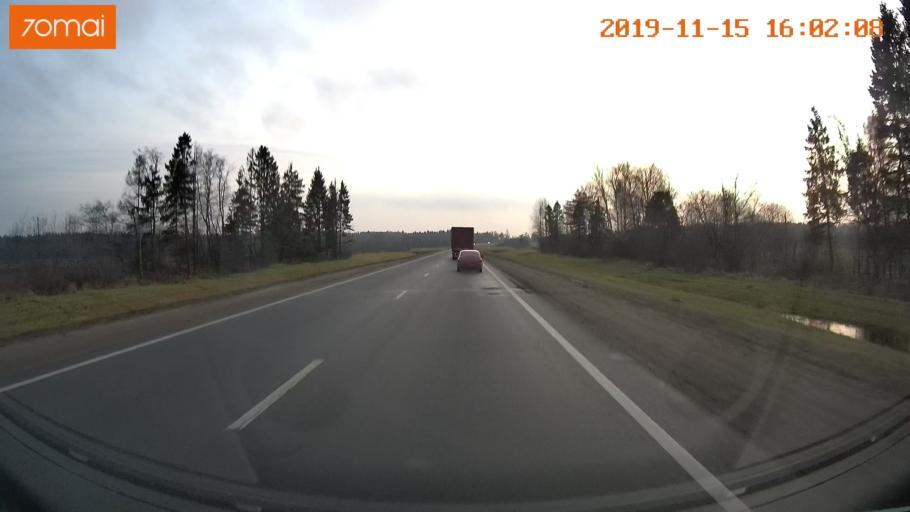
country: RU
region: Jaroslavl
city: Yaroslavl
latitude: 57.7747
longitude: 39.9266
